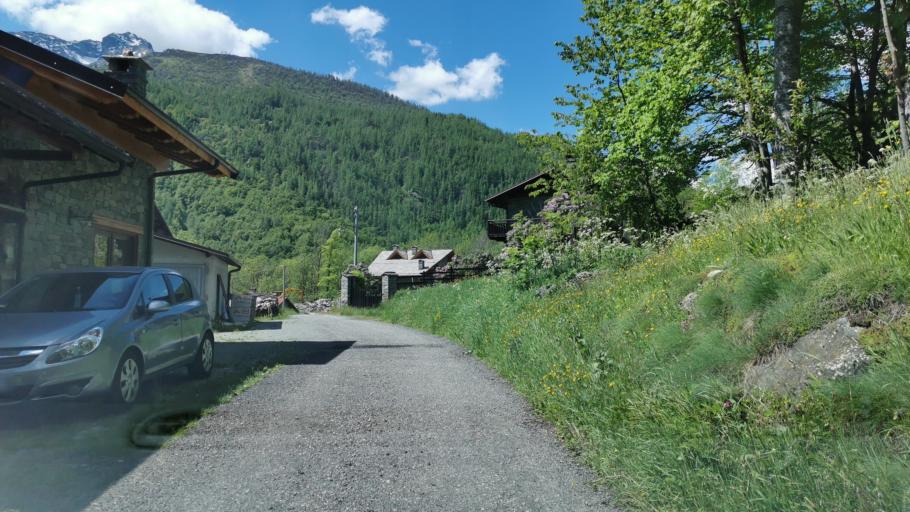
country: IT
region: Piedmont
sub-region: Provincia di Torino
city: Usseglio
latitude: 45.2340
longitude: 7.2313
